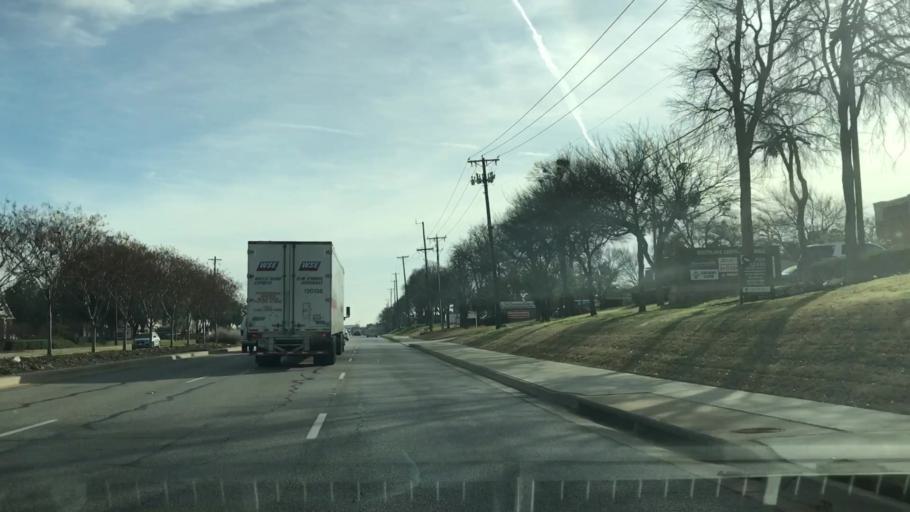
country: US
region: Texas
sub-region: Tarrant County
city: Southlake
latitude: 32.9403
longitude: -97.1148
